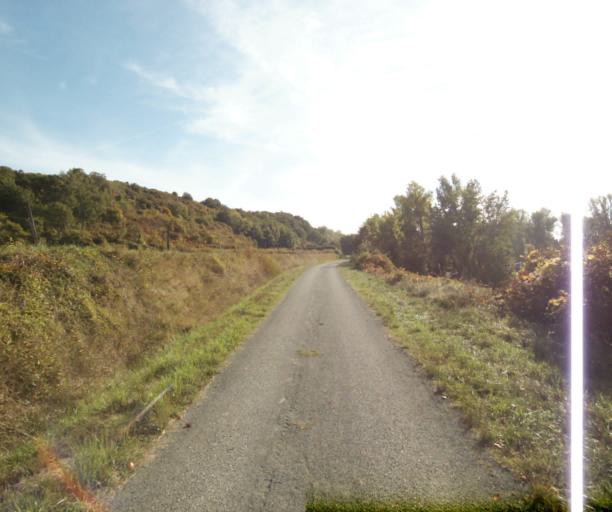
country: FR
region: Midi-Pyrenees
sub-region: Departement du Tarn-et-Garonne
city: Nohic
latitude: 43.9011
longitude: 1.4616
